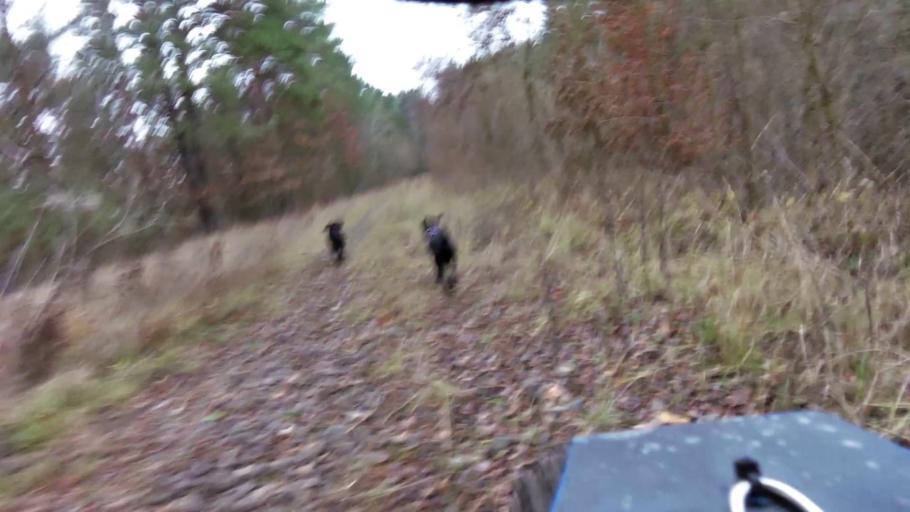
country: PL
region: Lubusz
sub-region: Powiat gorzowski
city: Jenin
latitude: 52.7188
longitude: 15.1262
